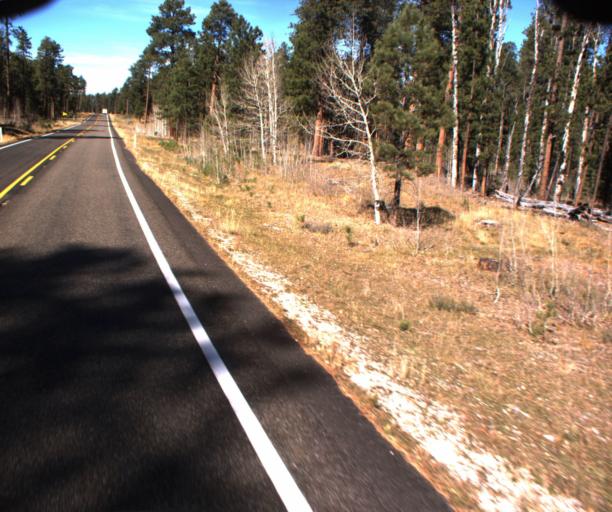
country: US
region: Arizona
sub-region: Coconino County
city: Fredonia
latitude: 36.6582
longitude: -112.1892
